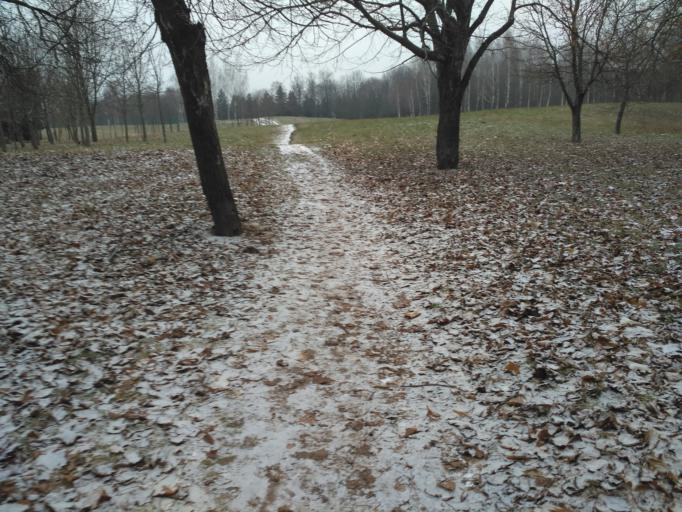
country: BY
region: Minsk
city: Novoye Medvezhino
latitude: 53.9170
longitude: 27.4859
